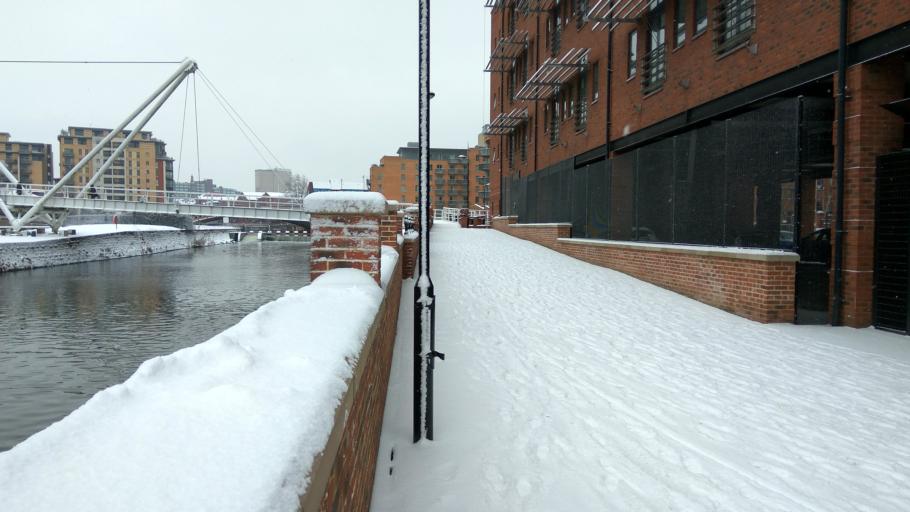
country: GB
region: England
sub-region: City and Borough of Leeds
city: Leeds
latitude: 53.7925
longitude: -1.5319
